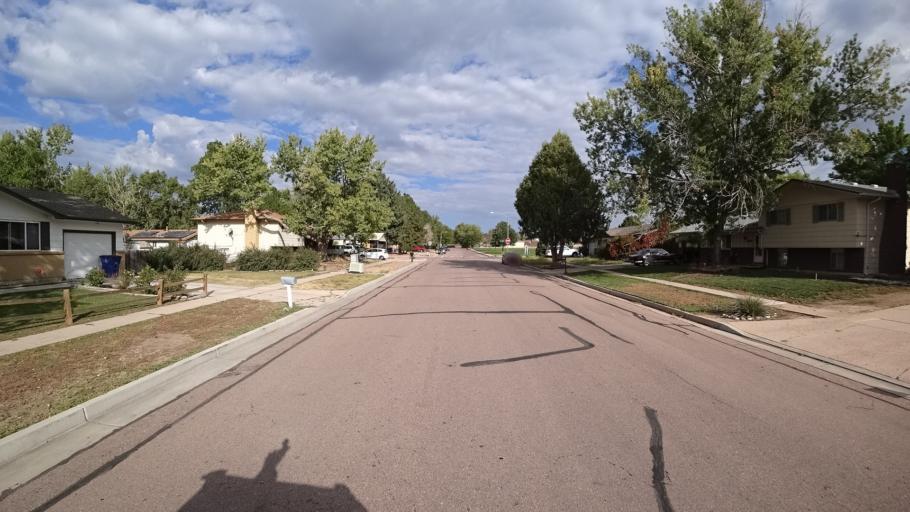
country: US
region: Colorado
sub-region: El Paso County
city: Cimarron Hills
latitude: 38.8506
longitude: -104.7443
